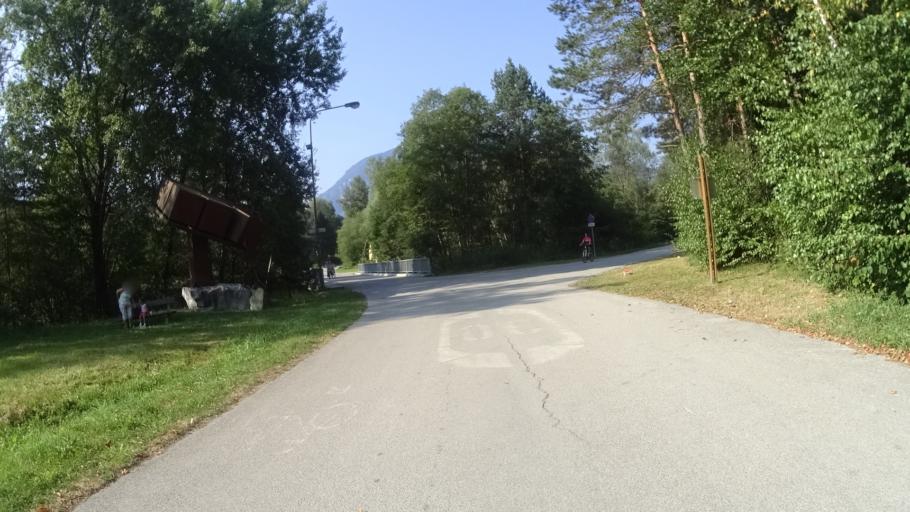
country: AT
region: Carinthia
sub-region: Politischer Bezirk Klagenfurt Land
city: Maria Rain
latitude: 46.5451
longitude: 14.2972
